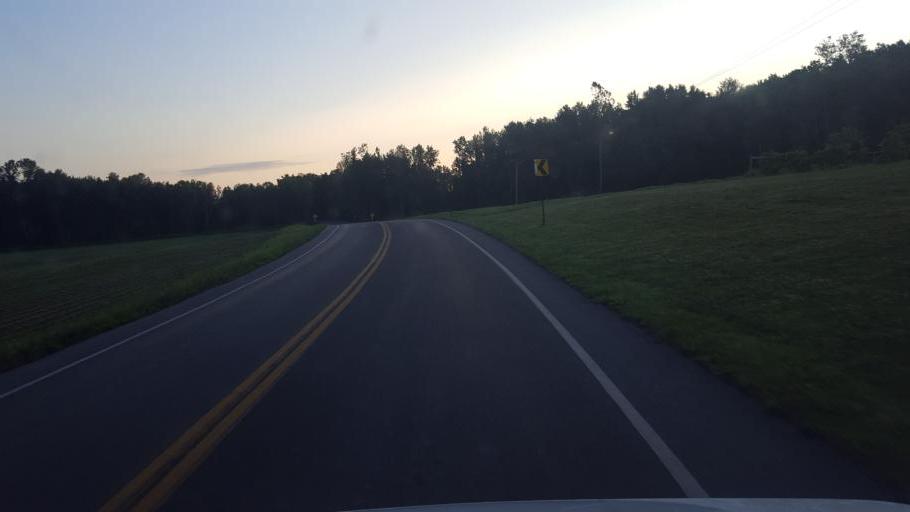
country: US
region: New York
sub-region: Wayne County
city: Clyde
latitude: 43.0652
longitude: -76.8916
